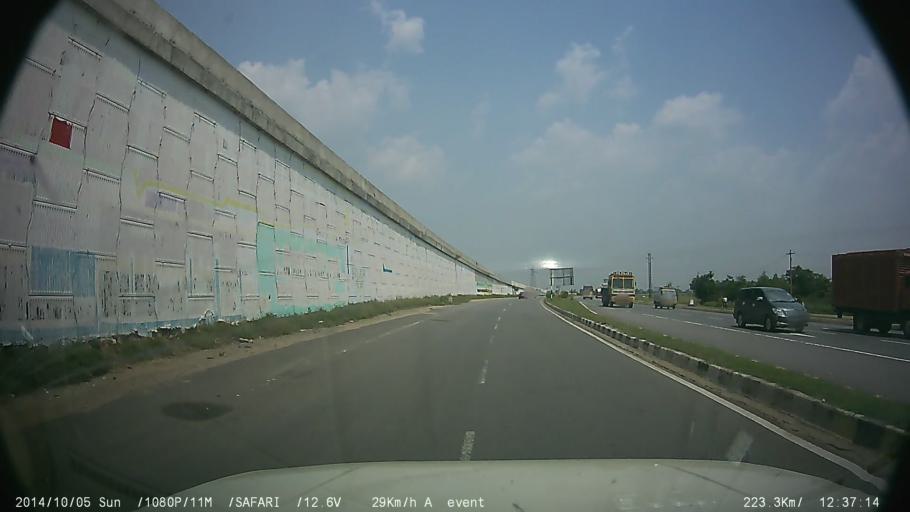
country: IN
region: Tamil Nadu
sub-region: Cuddalore
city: Vriddhachalam
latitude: 11.6773
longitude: 79.2734
